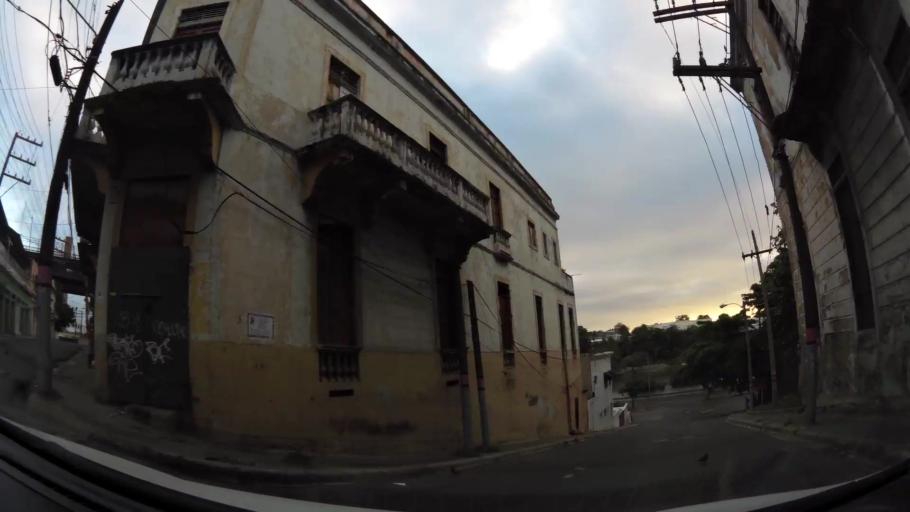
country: DO
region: Nacional
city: San Carlos
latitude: 18.4802
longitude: -69.8839
